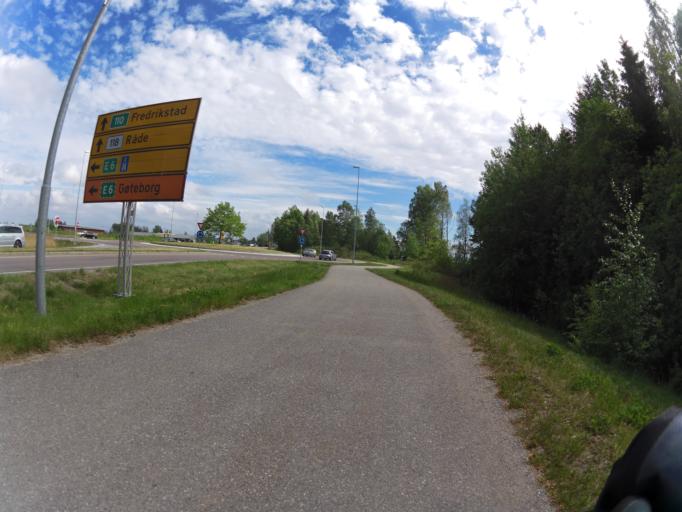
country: NO
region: Ostfold
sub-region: Rade
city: Karlshus
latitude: 59.3558
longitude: 10.8426
